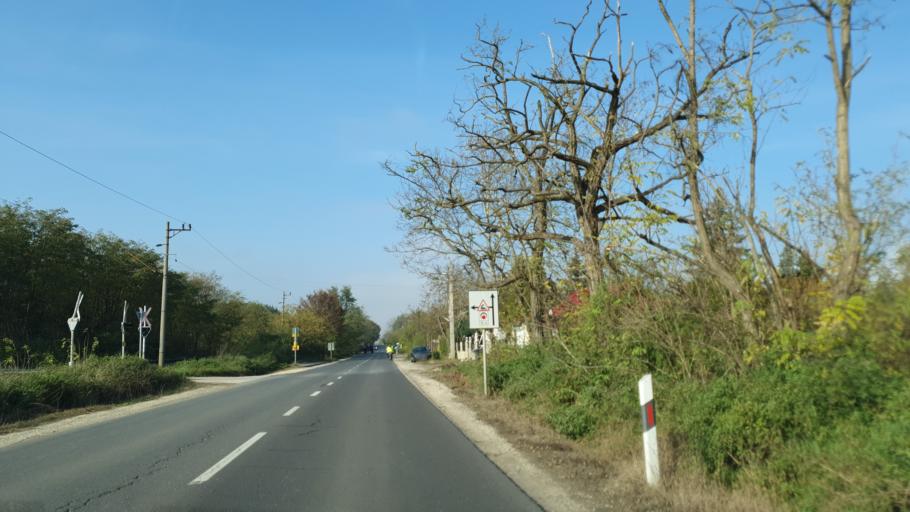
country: HU
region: Pest
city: Szod
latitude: 47.7385
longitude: 19.1900
